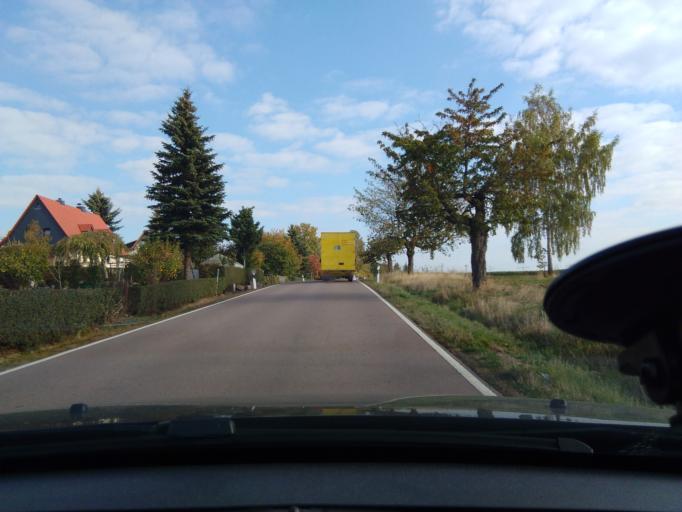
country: DE
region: Saxony
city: Nossen
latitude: 51.0625
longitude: 13.3104
